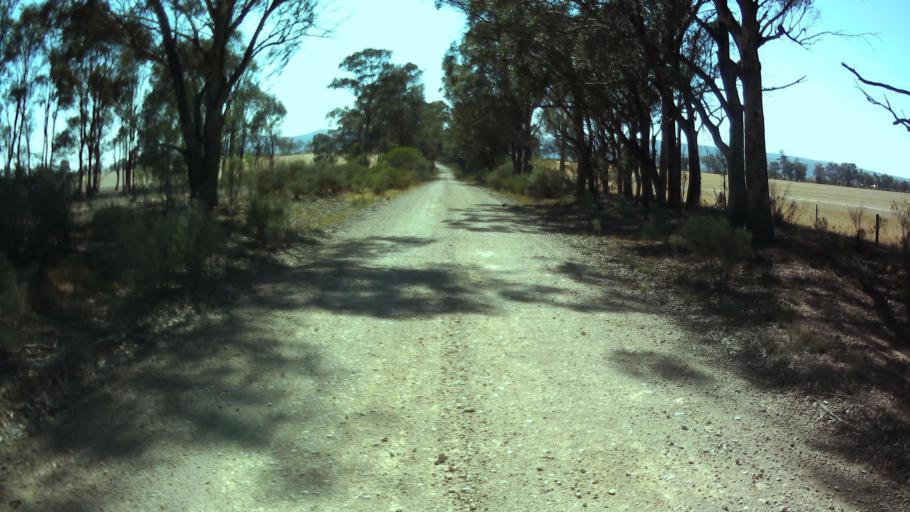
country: AU
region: New South Wales
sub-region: Weddin
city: Grenfell
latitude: -33.9016
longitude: 147.8699
